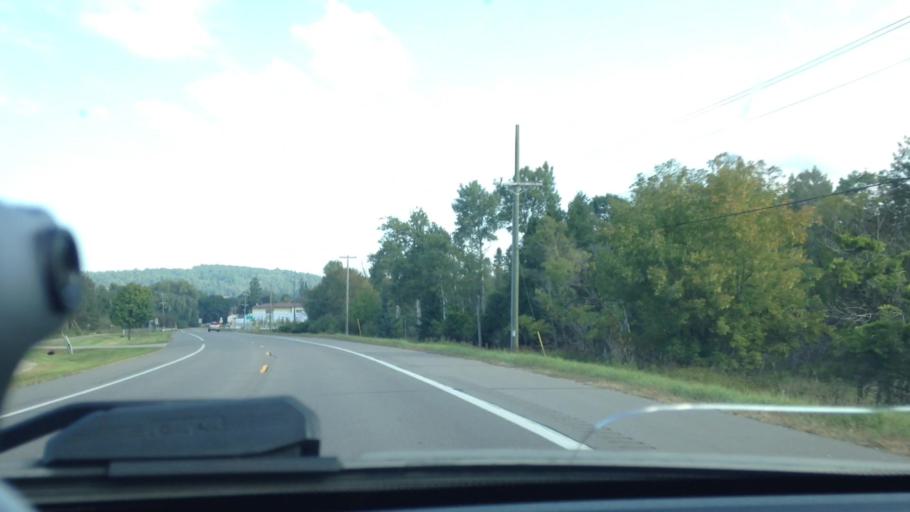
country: US
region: Michigan
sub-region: Dickinson County
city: Norway
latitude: 45.7780
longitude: -87.9090
